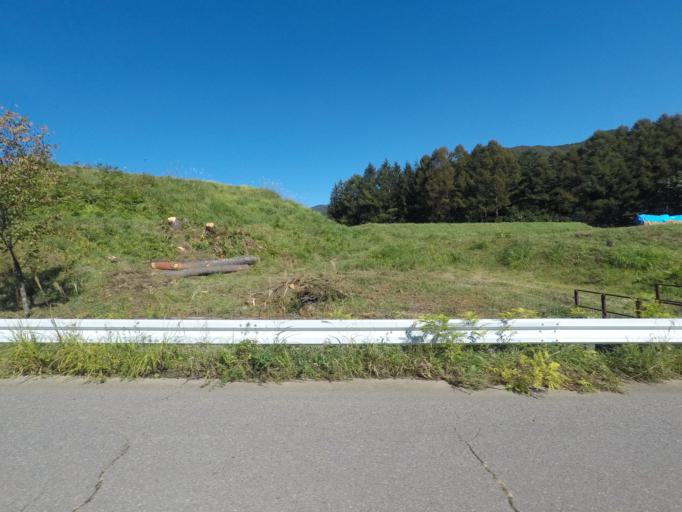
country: JP
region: Nagano
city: Tatsuno
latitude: 35.9753
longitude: 137.7457
